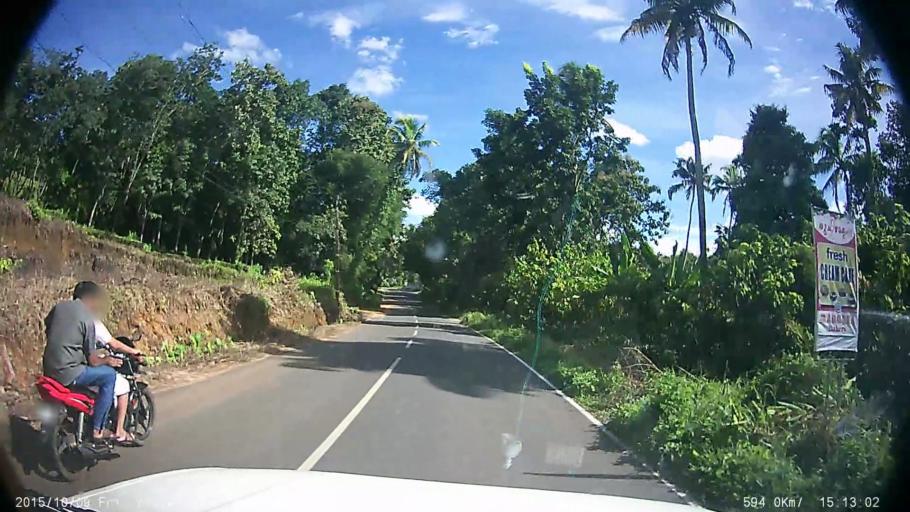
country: IN
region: Kerala
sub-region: Ernakulam
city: Piravam
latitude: 9.8681
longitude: 76.5885
